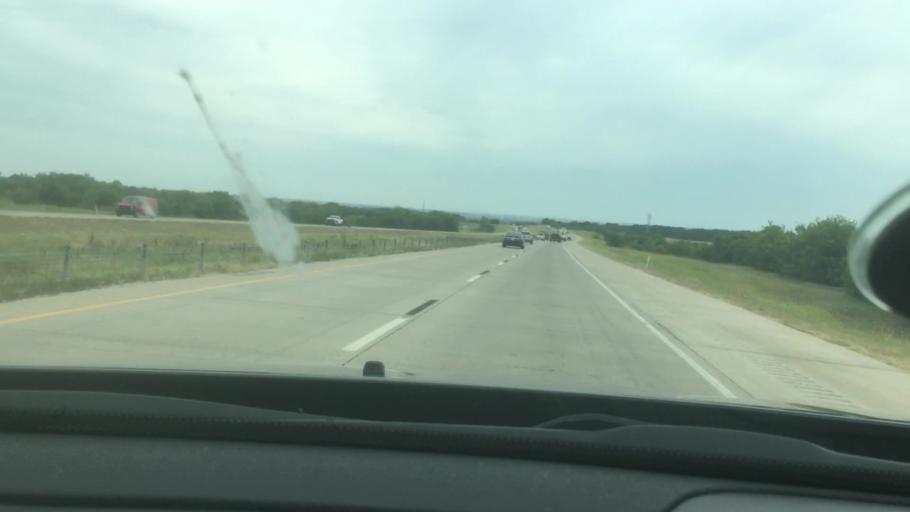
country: US
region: Oklahoma
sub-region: Carter County
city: Ardmore
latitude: 34.2225
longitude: -97.1630
